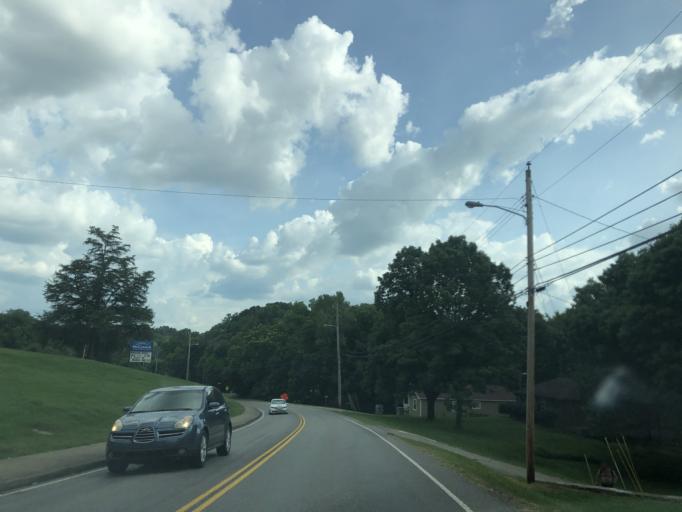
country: US
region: Tennessee
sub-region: Davidson County
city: Lakewood
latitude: 36.1607
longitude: -86.6815
